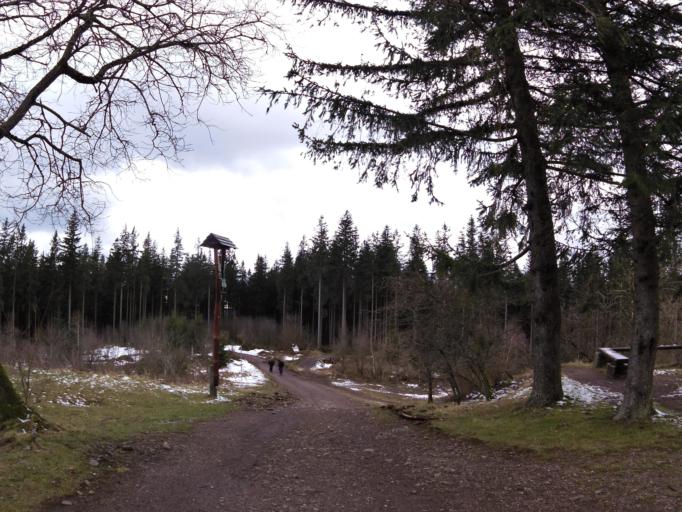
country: DE
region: Thuringia
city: Ilmenau
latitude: 50.6664
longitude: 10.9072
